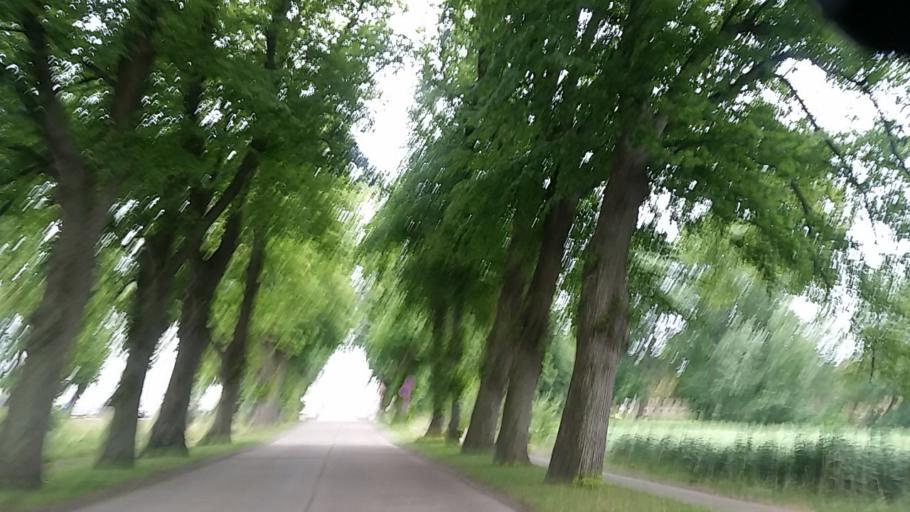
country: DE
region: Schleswig-Holstein
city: Busdorf
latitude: 54.5100
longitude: 9.5417
